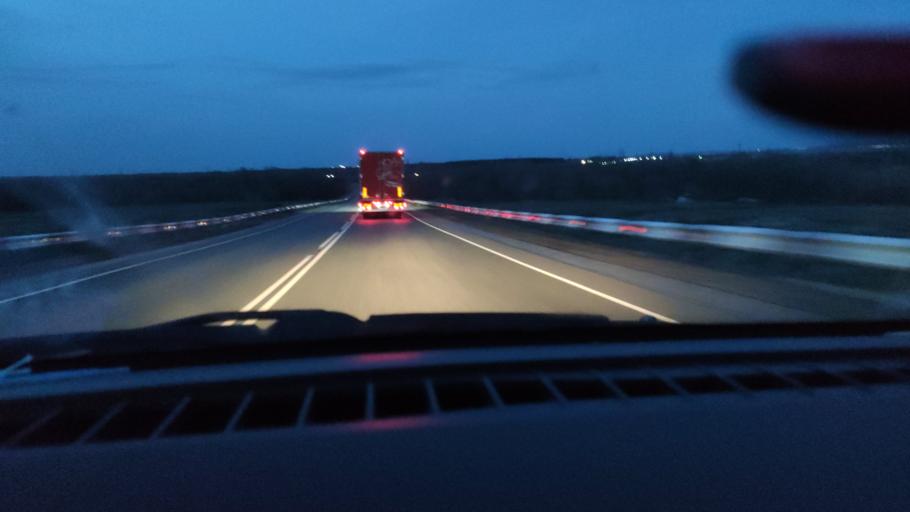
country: RU
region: Saratov
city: Sennoy
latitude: 52.1412
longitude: 46.8900
